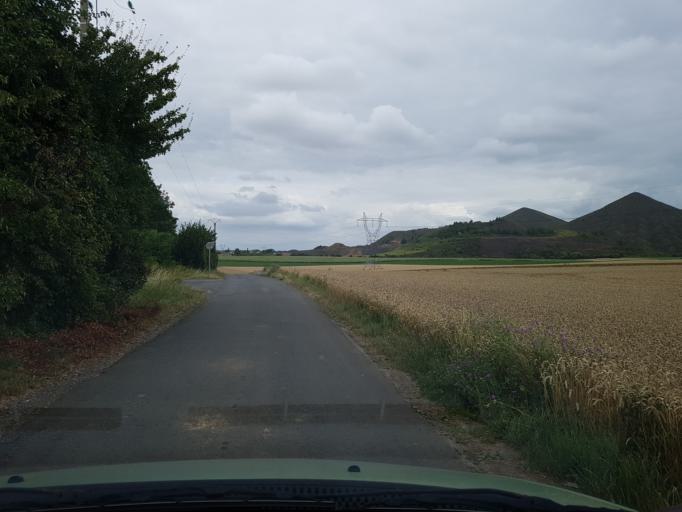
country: FR
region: Nord-Pas-de-Calais
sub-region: Departement du Pas-de-Calais
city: Grenay
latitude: 50.4435
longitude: 2.7614
